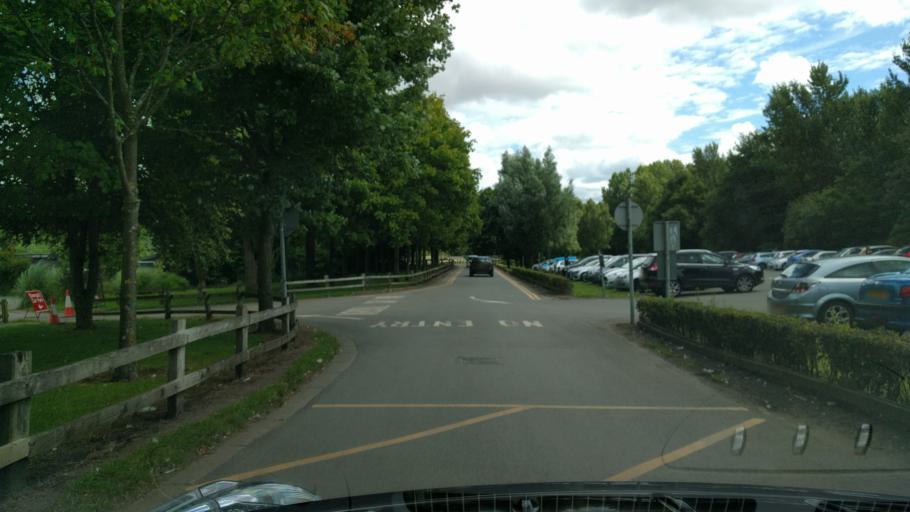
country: GB
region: England
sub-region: Borough of Wigan
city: Leigh
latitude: 53.4864
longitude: -2.5368
